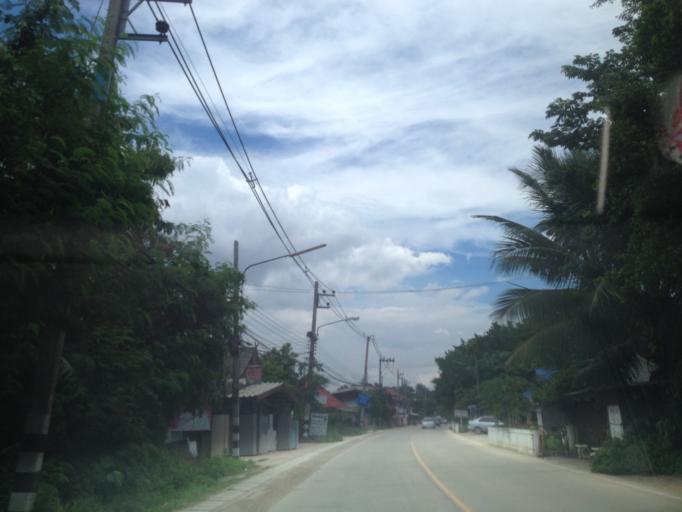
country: TH
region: Chiang Mai
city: Chiang Mai
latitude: 18.7517
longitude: 98.9875
